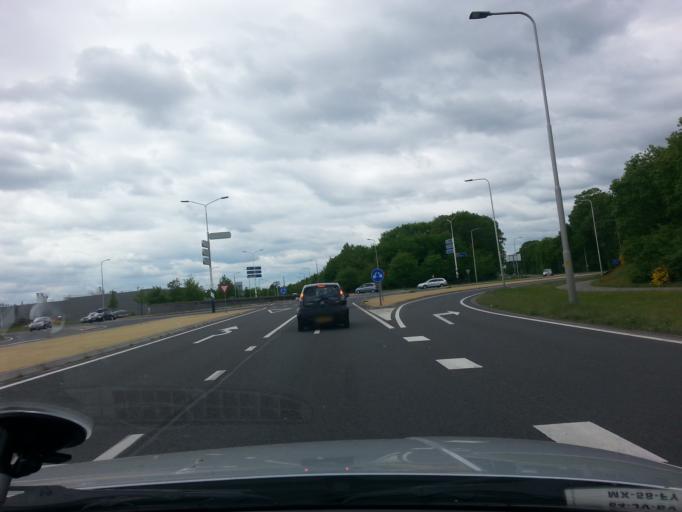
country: NL
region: Overijssel
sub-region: Gemeente Oldenzaal
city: Oldenzaal
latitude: 52.3009
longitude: 6.8969
